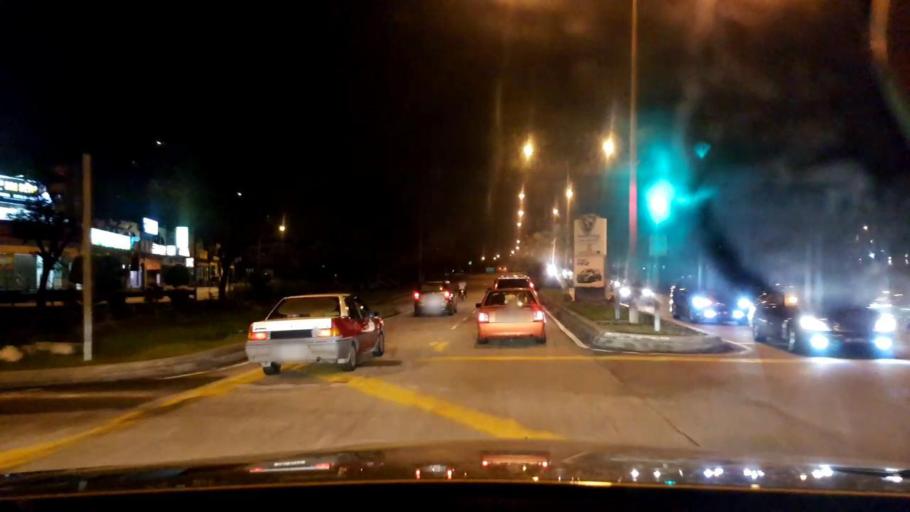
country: MY
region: Selangor
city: Subang Jaya
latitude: 3.0448
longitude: 101.5758
